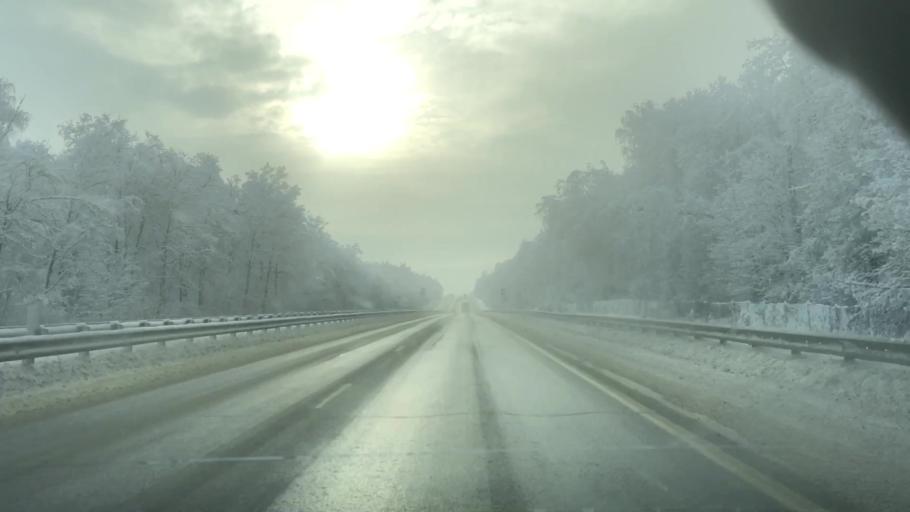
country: RU
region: Tula
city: Venev
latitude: 54.3654
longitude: 38.1547
